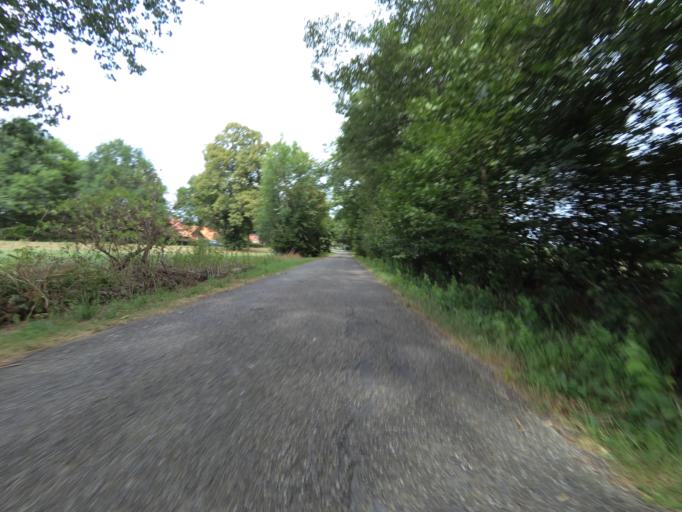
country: DE
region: North Rhine-Westphalia
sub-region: Regierungsbezirk Munster
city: Ahaus
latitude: 52.1286
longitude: 7.0052
